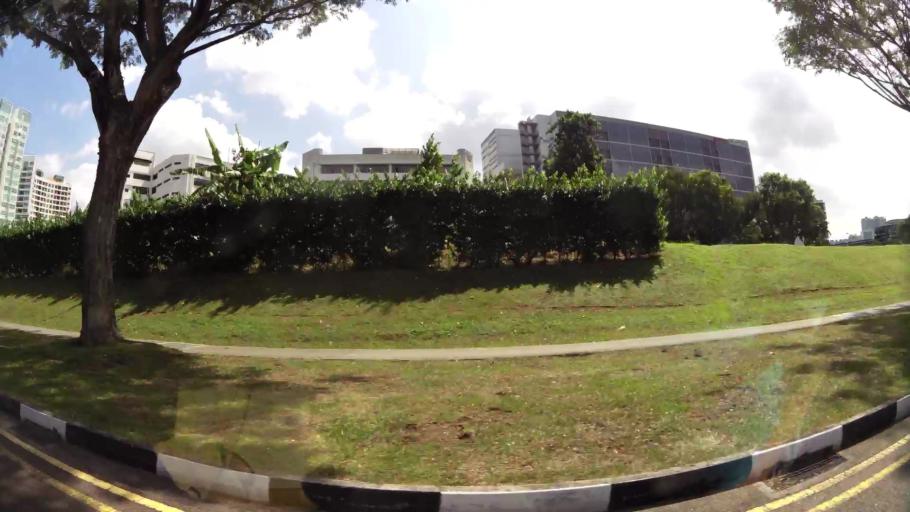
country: SG
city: Singapore
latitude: 1.3492
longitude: 103.8396
